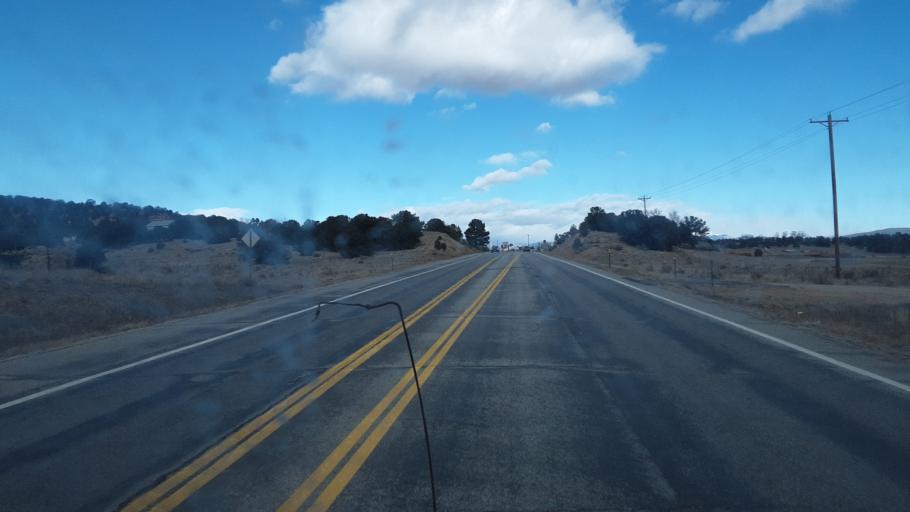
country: US
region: Colorado
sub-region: Chaffee County
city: Salida
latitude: 38.6725
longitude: -106.0912
